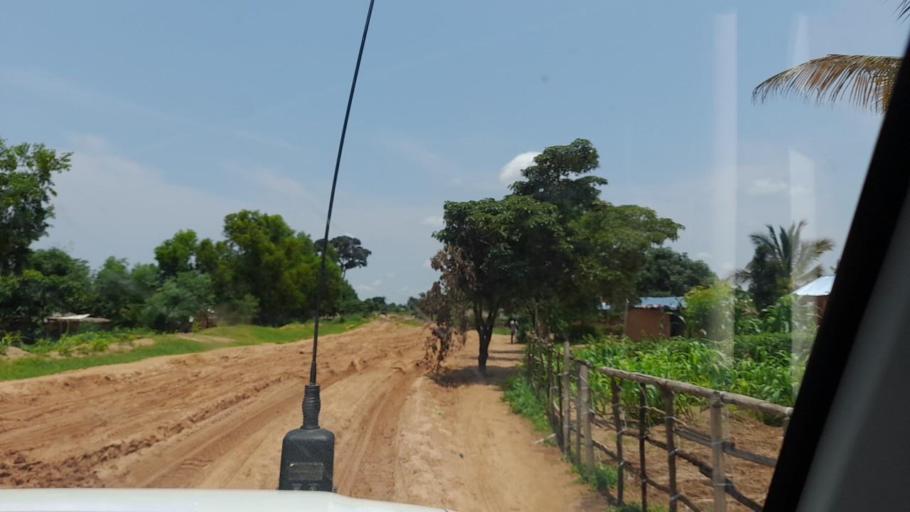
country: CD
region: Kasai-Occidental
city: Kananga
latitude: -5.9486
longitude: 22.2780
